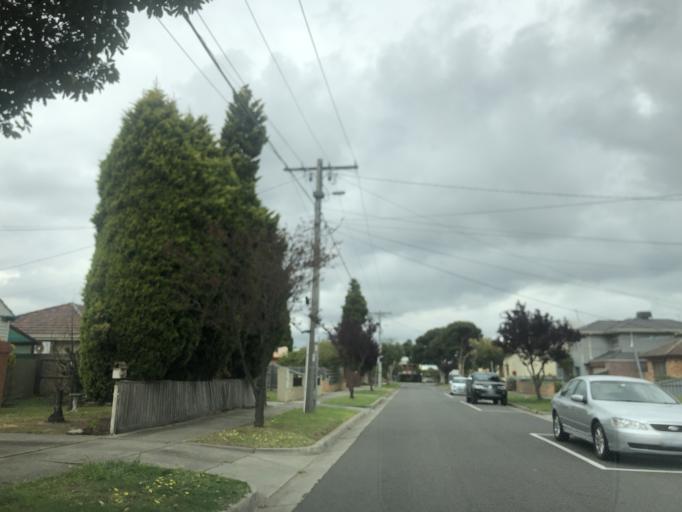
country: AU
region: Victoria
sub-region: Greater Dandenong
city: Dandenong North
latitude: -37.9691
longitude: 145.2018
